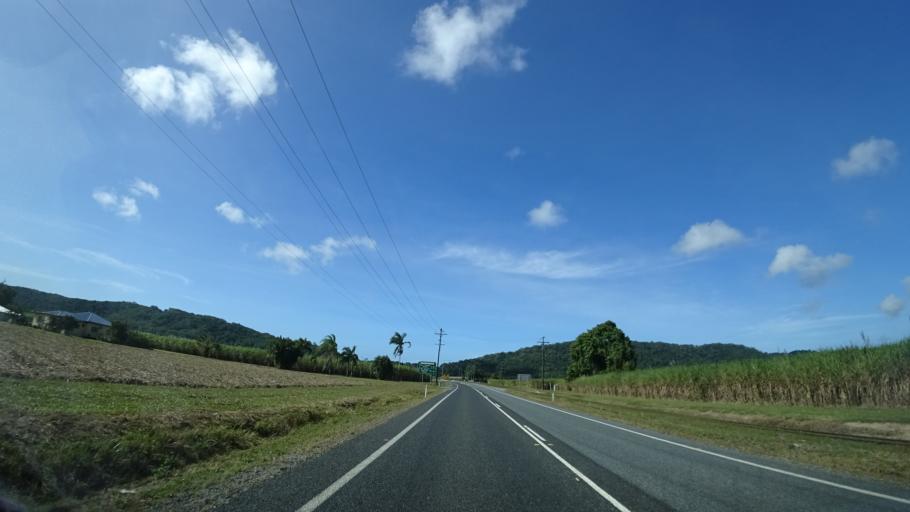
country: AU
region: Queensland
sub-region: Cairns
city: Port Douglas
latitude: -16.4834
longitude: 145.3874
